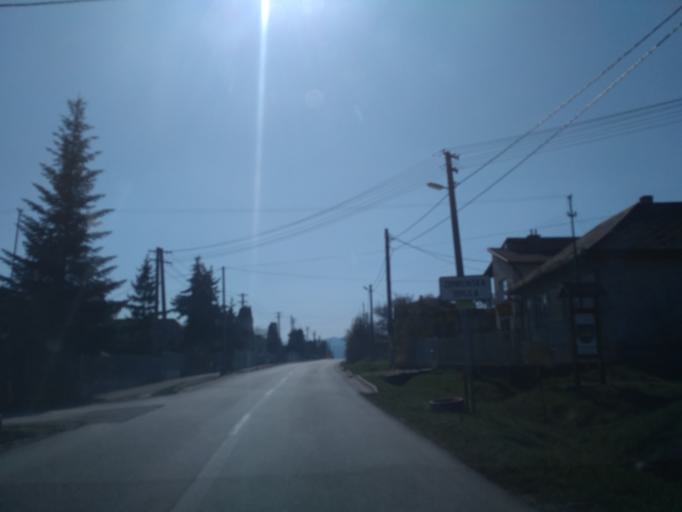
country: SK
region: Kosicky
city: Secovce
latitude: 48.6490
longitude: 21.5782
